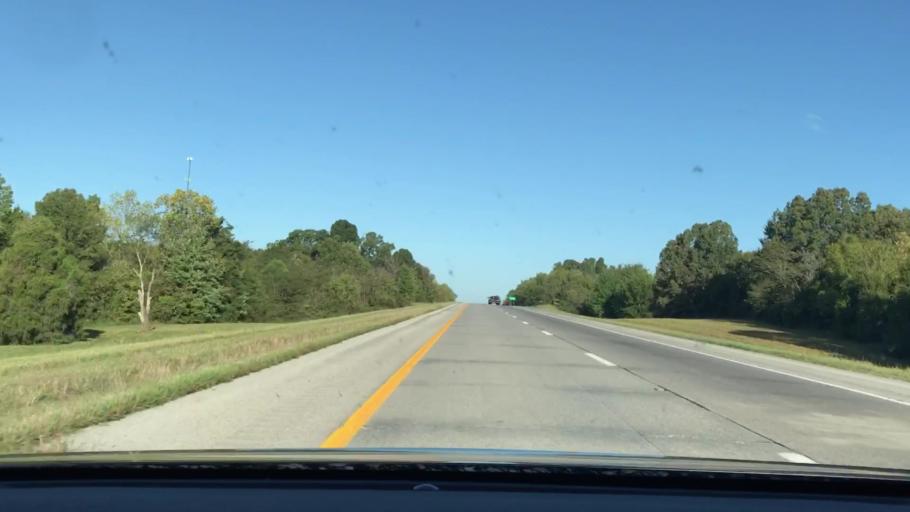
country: US
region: Kentucky
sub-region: Trigg County
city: Cadiz
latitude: 36.9523
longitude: -87.8440
